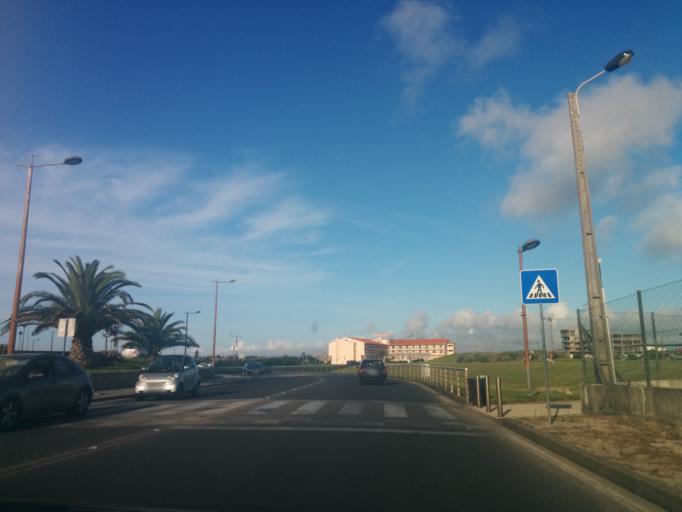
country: PT
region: Leiria
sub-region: Peniche
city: Peniche
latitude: 39.3576
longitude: -9.3676
